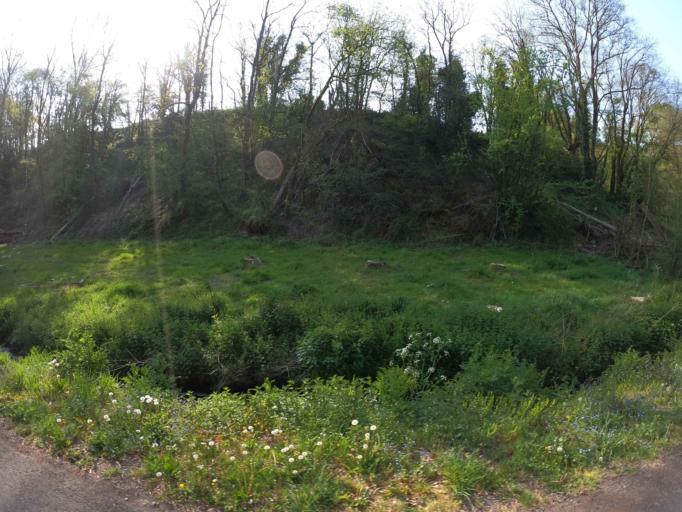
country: FR
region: Pays de la Loire
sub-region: Departement de Maine-et-Loire
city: La Romagne
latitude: 47.0664
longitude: -1.0091
